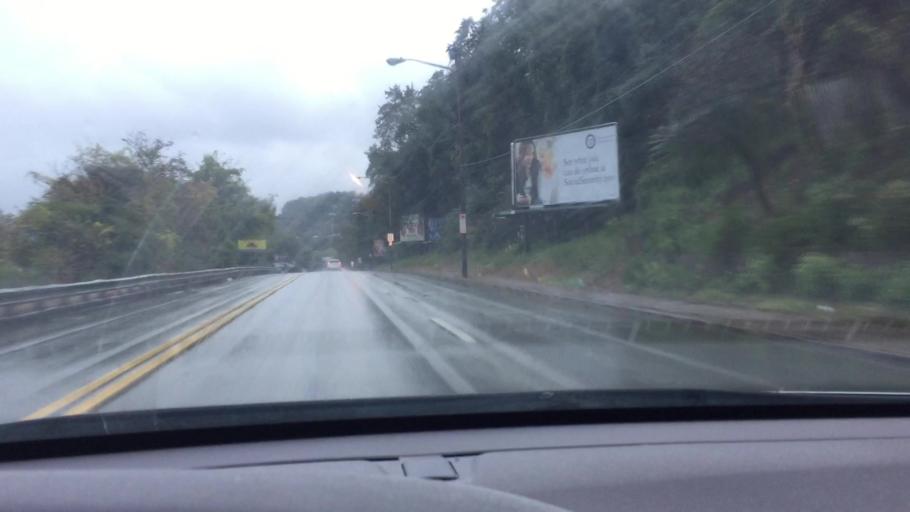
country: US
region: Pennsylvania
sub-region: Allegheny County
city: Mount Oliver
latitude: 40.4216
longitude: -79.9498
